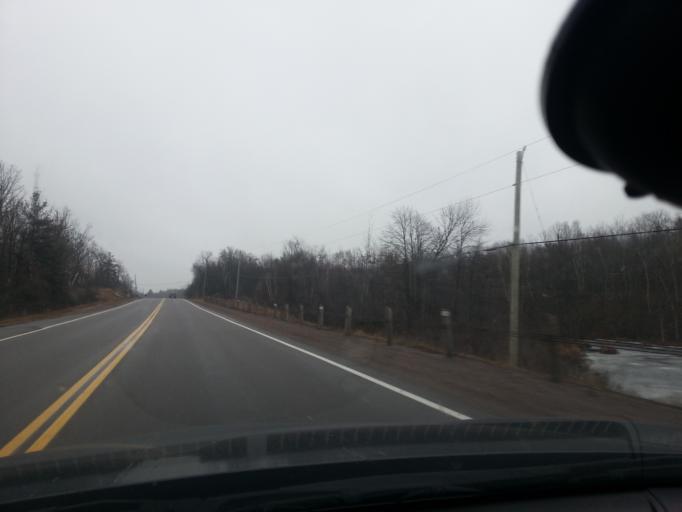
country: CA
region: Ontario
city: Deseronto
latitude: 44.5640
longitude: -77.2240
